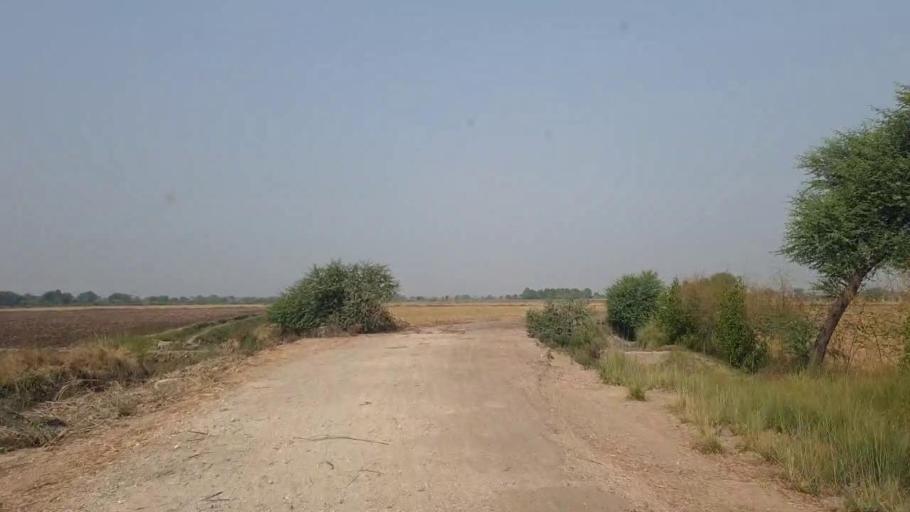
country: PK
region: Sindh
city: Matli
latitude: 25.1492
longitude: 68.7296
